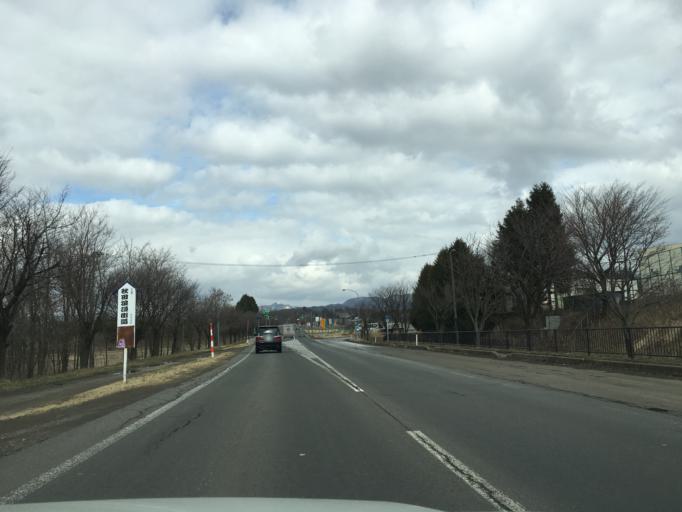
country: JP
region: Akita
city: Hanawa
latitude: 40.2551
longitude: 140.7607
